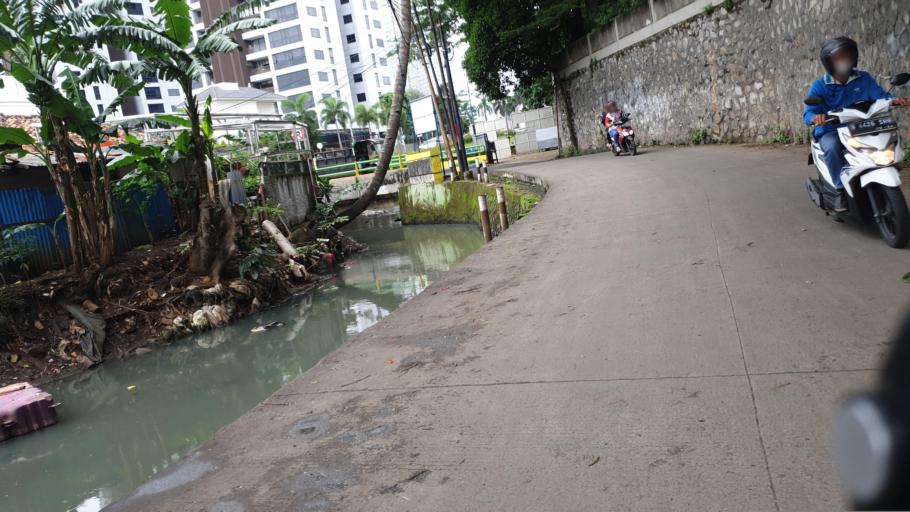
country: ID
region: Jakarta Raya
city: Jakarta
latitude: -6.2467
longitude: 106.7884
